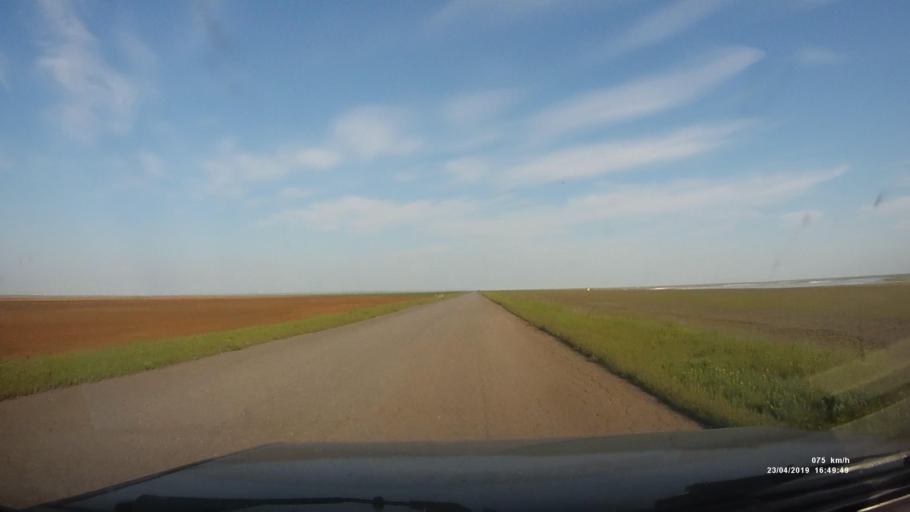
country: RU
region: Kalmykiya
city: Priyutnoye
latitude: 46.3295
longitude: 43.2823
